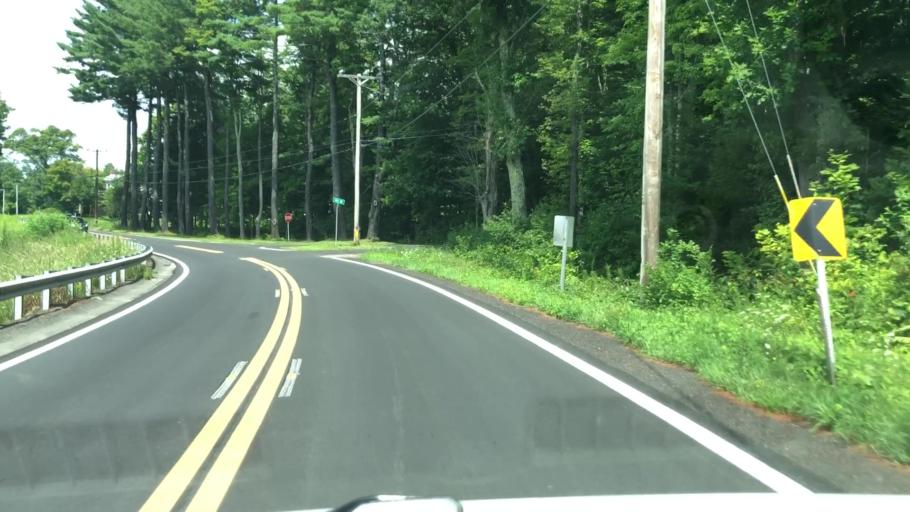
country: US
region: Massachusetts
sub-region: Franklin County
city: Ashfield
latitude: 42.5129
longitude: -72.7750
